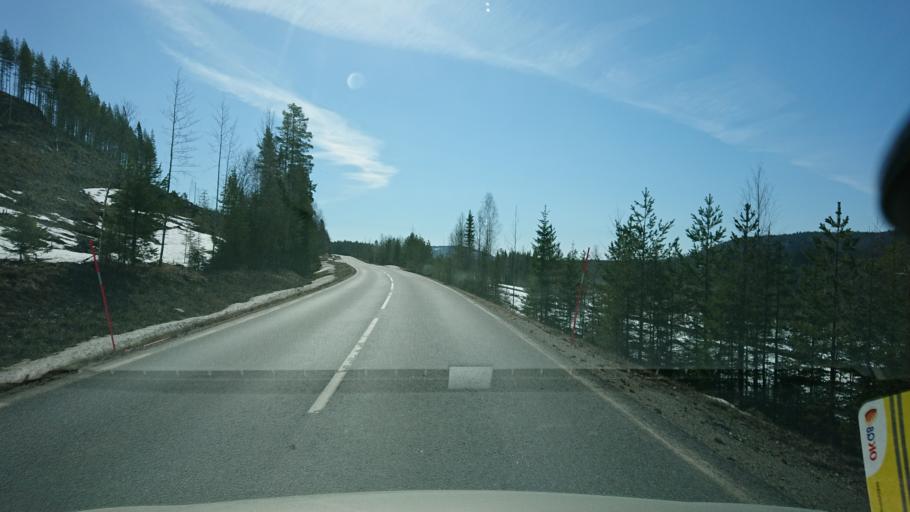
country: SE
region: Vaesterbotten
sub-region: Dorotea Kommun
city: Dorotea
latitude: 64.0385
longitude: 16.2601
